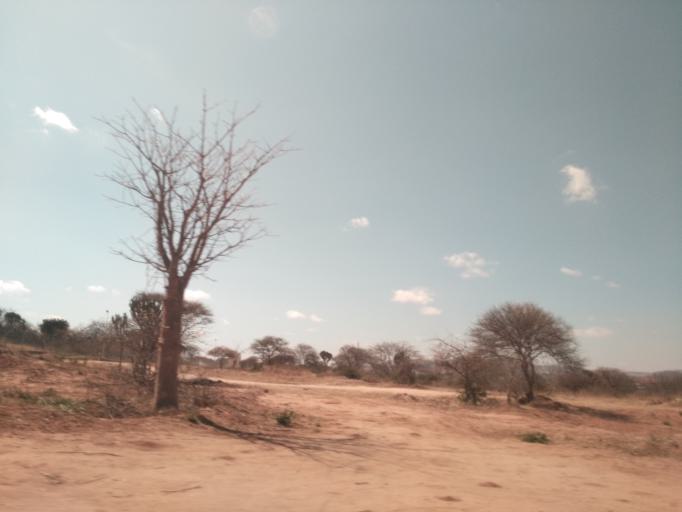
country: TZ
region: Dodoma
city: Dodoma
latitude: -6.1561
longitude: 35.7587
